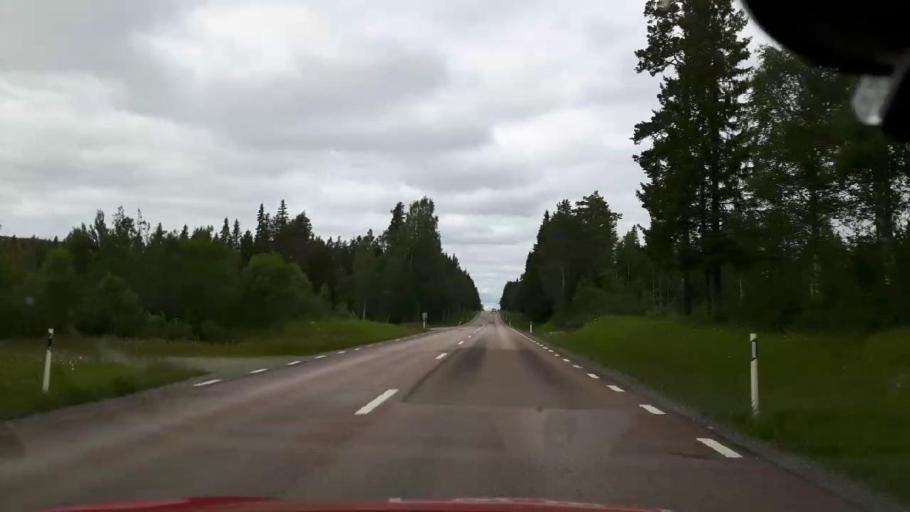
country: SE
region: Jaemtland
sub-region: OEstersunds Kommun
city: Brunflo
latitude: 62.9820
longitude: 14.9985
